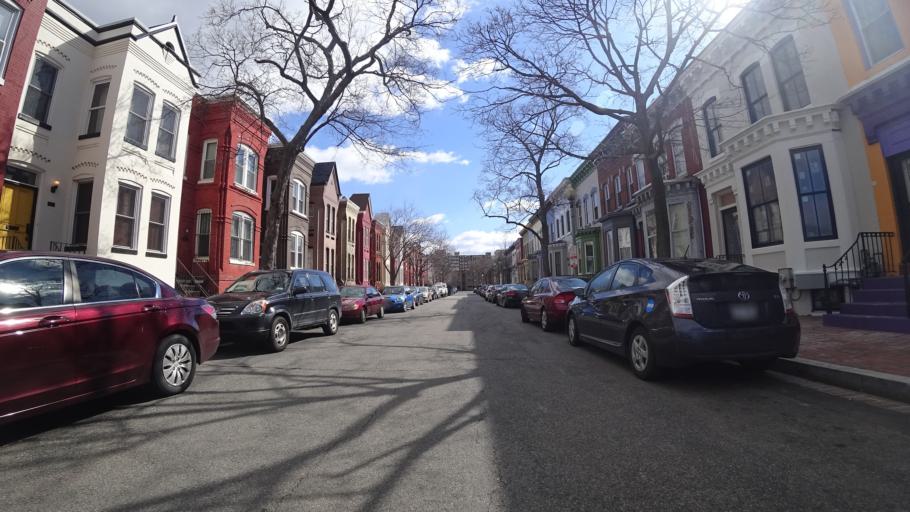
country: US
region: Washington, D.C.
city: Washington, D.C.
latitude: 38.9134
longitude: -77.0257
